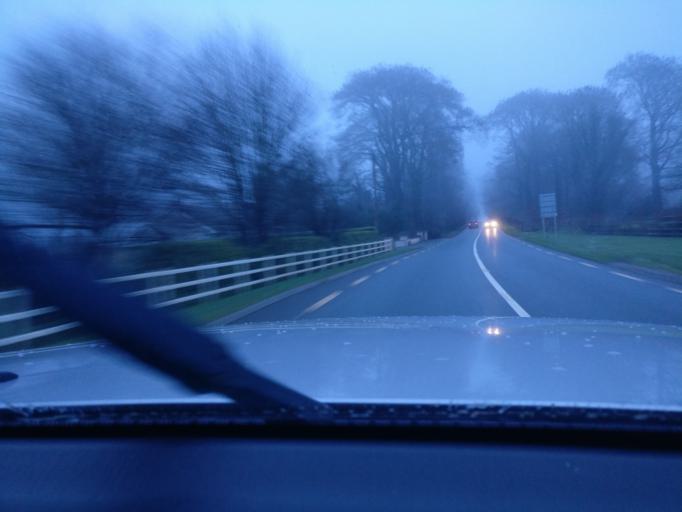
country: IE
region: Leinster
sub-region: An Mhi
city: Athboy
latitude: 53.6388
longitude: -6.8914
